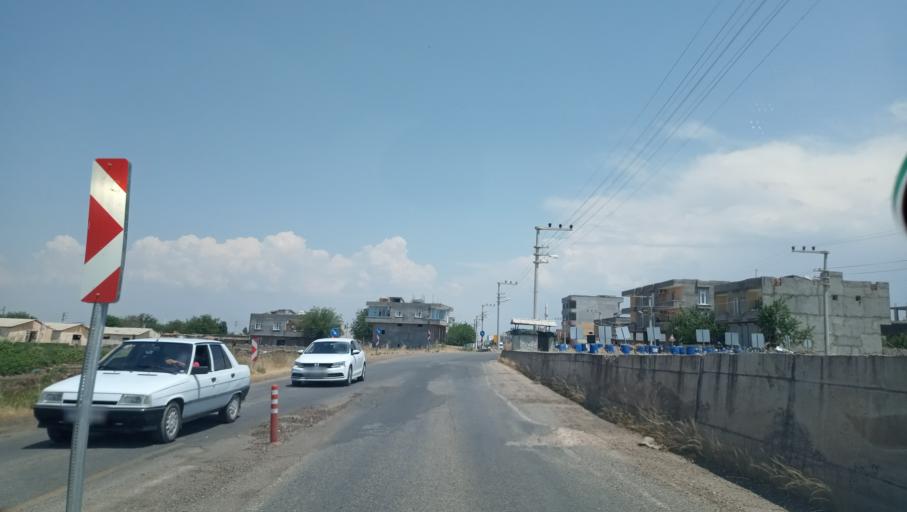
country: TR
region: Diyarbakir
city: Tepe
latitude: 37.7932
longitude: 40.7612
